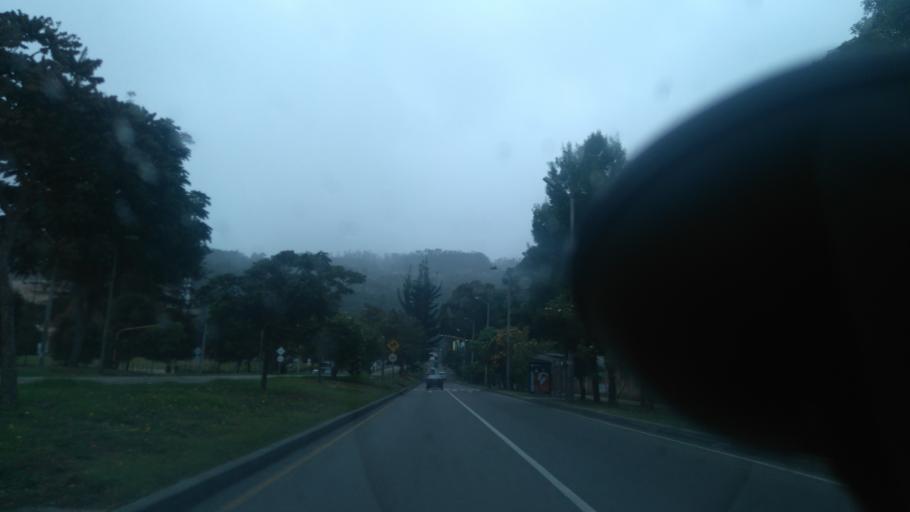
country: CO
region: Cundinamarca
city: La Calera
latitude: 4.7474
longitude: -74.0275
